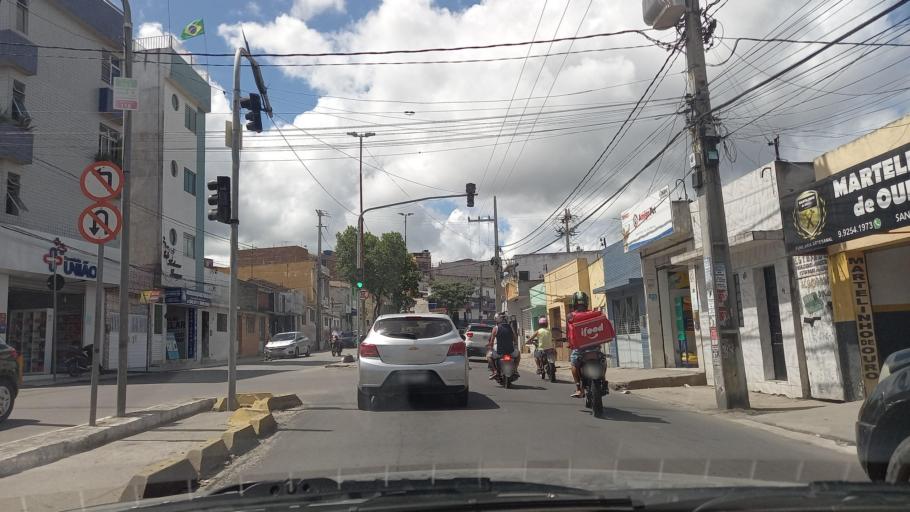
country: BR
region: Pernambuco
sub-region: Caruaru
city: Caruaru
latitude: -8.2829
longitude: -35.9627
